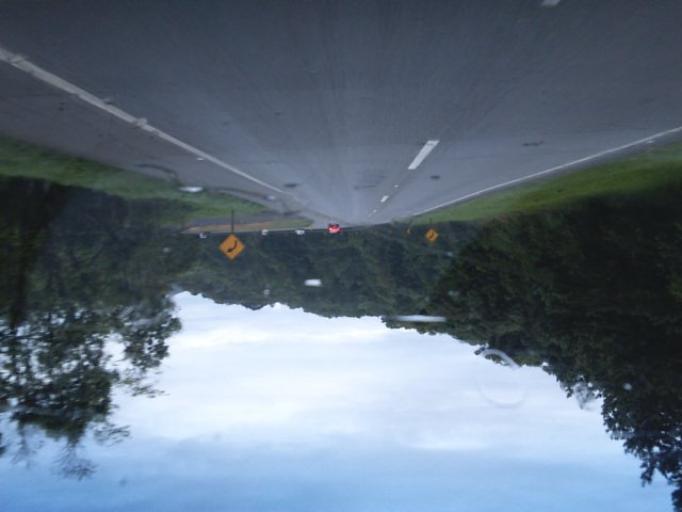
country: BR
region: Parana
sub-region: Sao Jose Dos Pinhais
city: Sao Jose dos Pinhais
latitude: -25.8517
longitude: -49.0046
